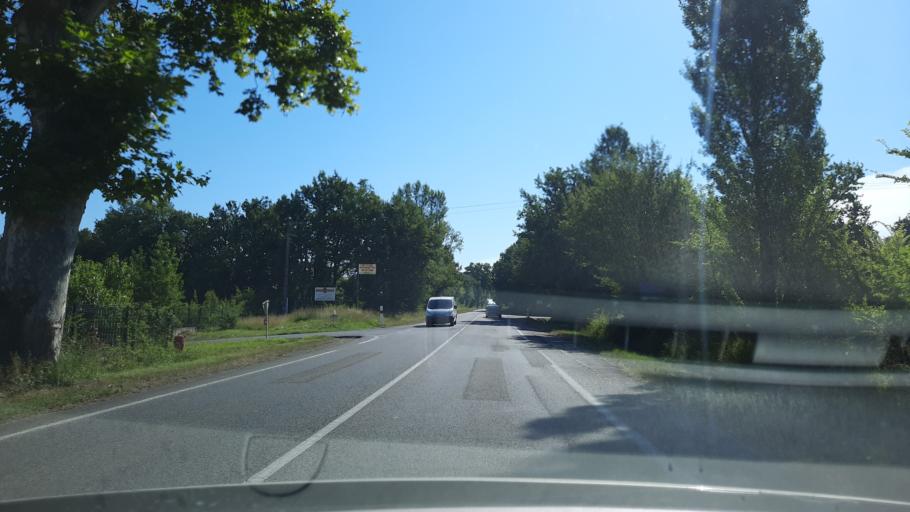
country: FR
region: Midi-Pyrenees
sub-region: Departement du Tarn-et-Garonne
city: Monteils
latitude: 44.1664
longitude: 1.5672
